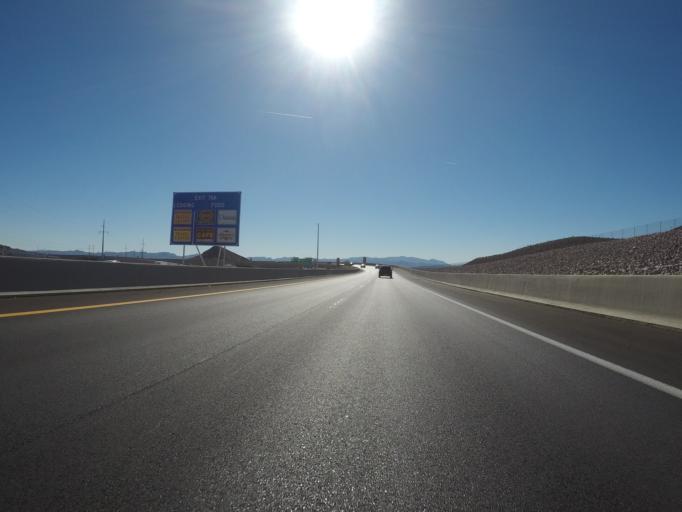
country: US
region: Nevada
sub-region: Clark County
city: Boulder City
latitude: 35.9721
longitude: -114.9144
